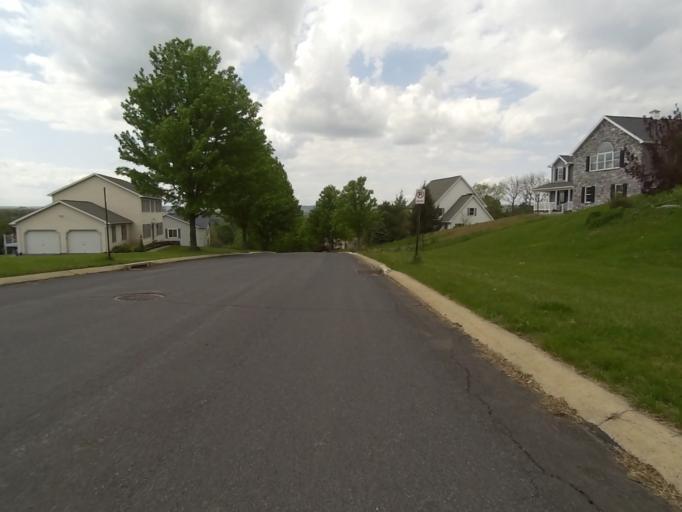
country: US
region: Pennsylvania
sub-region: Centre County
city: Lemont
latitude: 40.8070
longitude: -77.8130
